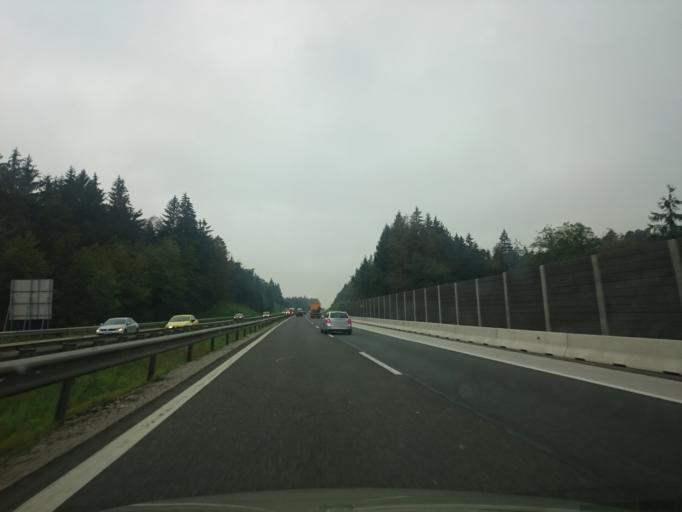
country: SI
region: Celje
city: Ljubecna
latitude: 46.2555
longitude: 15.3512
